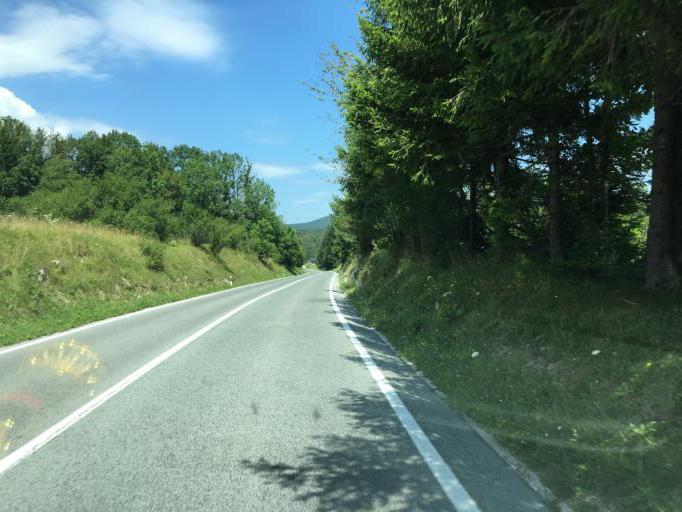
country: HR
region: Licko-Senjska
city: Jezerce
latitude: 44.8569
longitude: 15.6491
